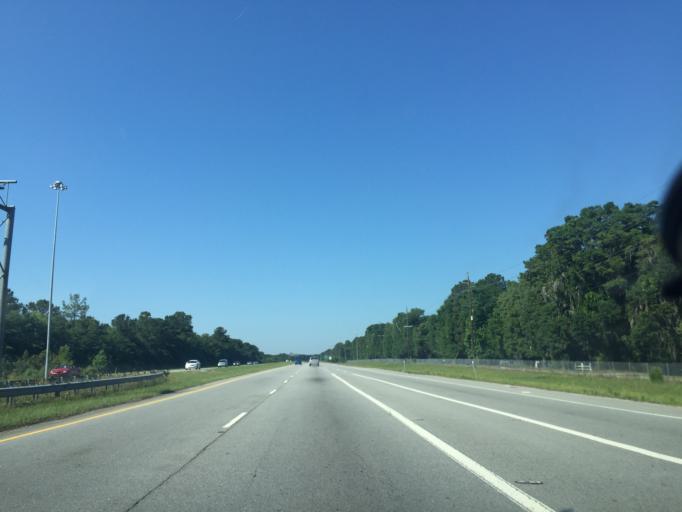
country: US
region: Georgia
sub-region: Chatham County
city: Isle of Hope
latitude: 31.9872
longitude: -81.0854
